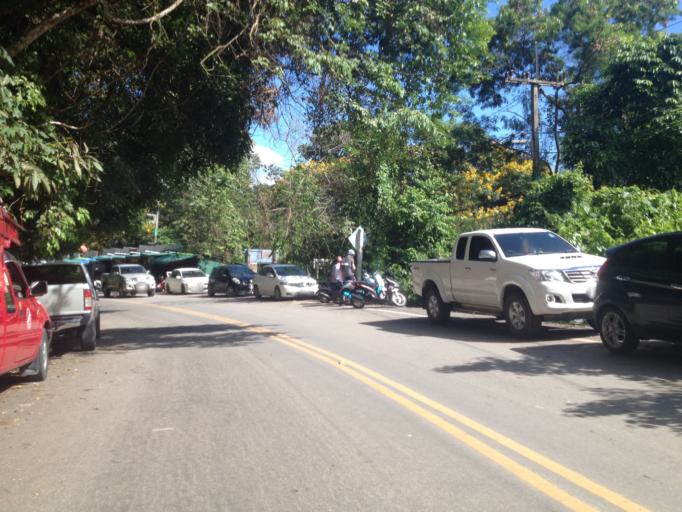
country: TH
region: Chiang Mai
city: Chiang Mai
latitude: 18.8044
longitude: 98.9182
